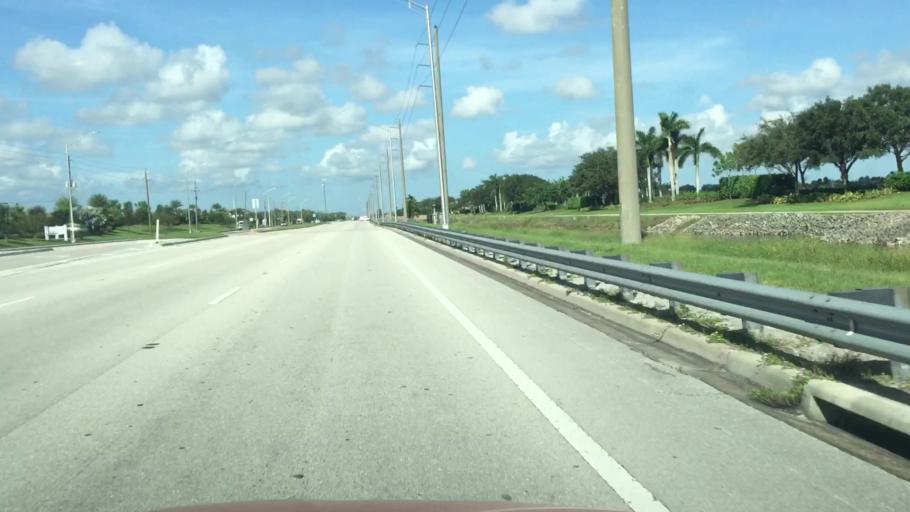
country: US
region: Florida
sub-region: Collier County
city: Vineyards
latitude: 26.2733
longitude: -81.6689
